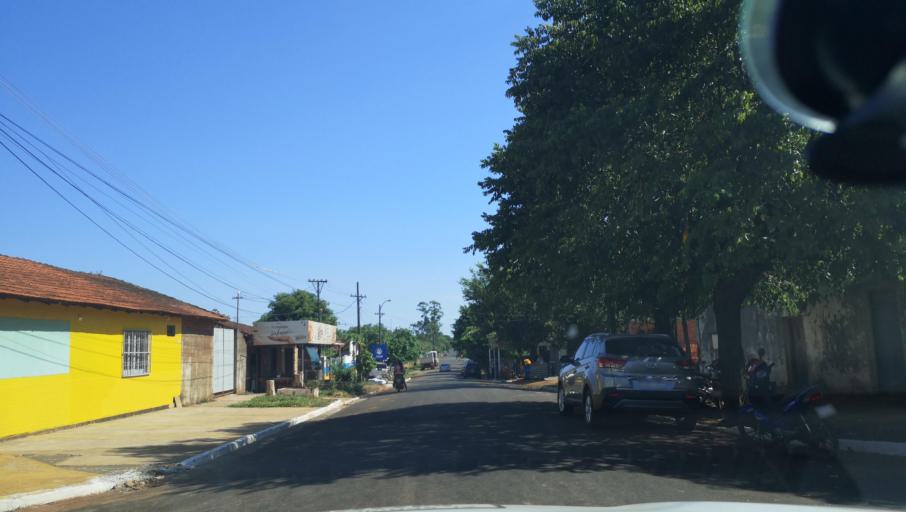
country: PY
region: Itapua
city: Carmen del Parana
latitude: -27.1694
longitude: -56.2322
